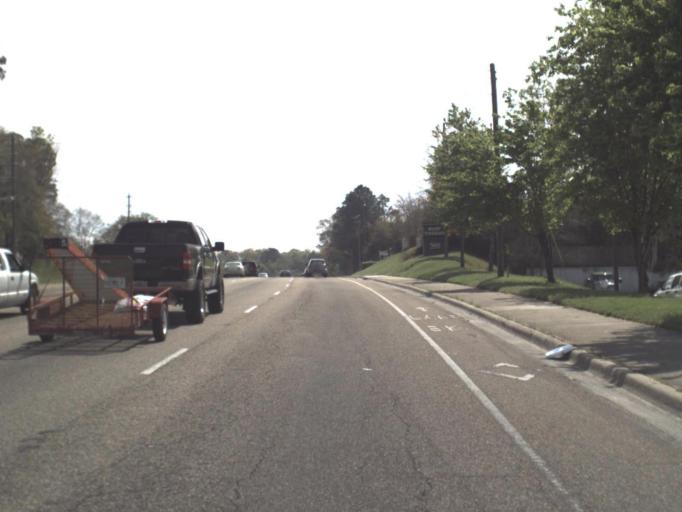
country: US
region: Florida
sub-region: Leon County
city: Tallahassee
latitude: 30.4746
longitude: -84.2350
